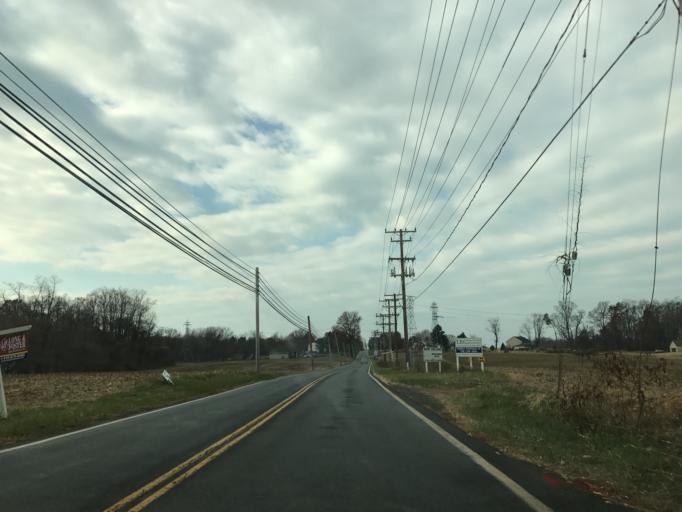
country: US
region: Maryland
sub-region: Harford County
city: Jarrettsville
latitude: 39.6087
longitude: -76.4610
